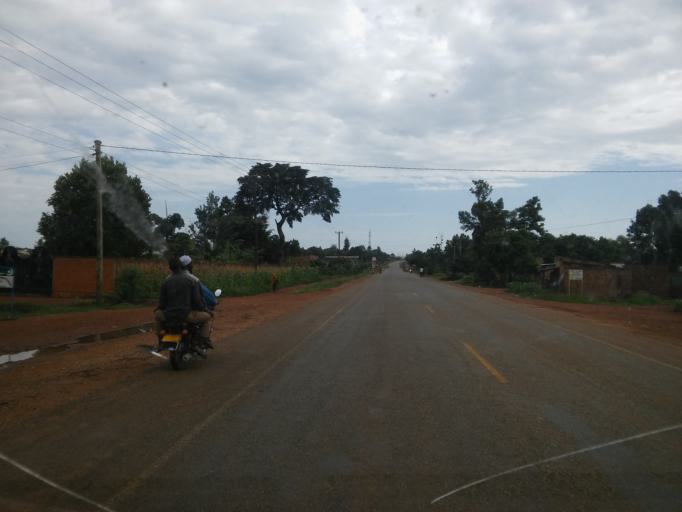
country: UG
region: Eastern Region
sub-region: Mbale District
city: Mbale
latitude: 1.1335
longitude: 34.1662
